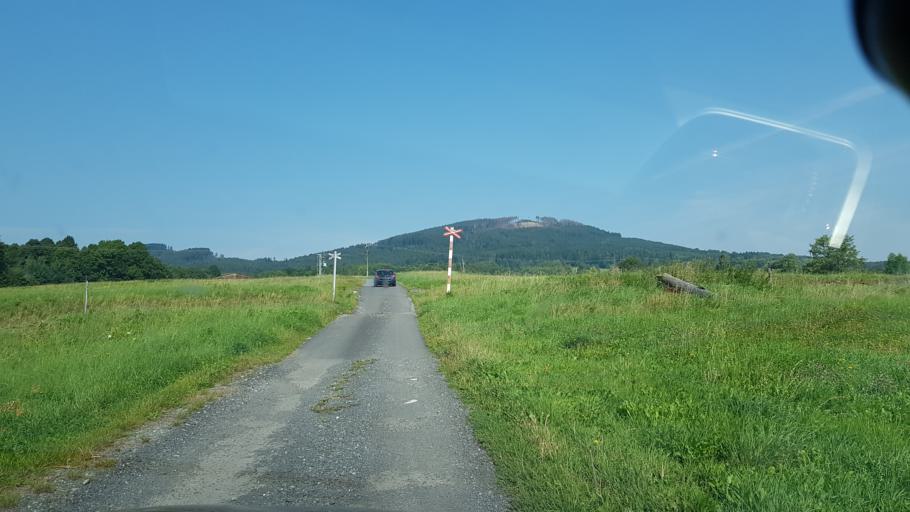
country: CZ
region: Olomoucky
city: Ceska Ves
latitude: 50.2664
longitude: 17.2388
